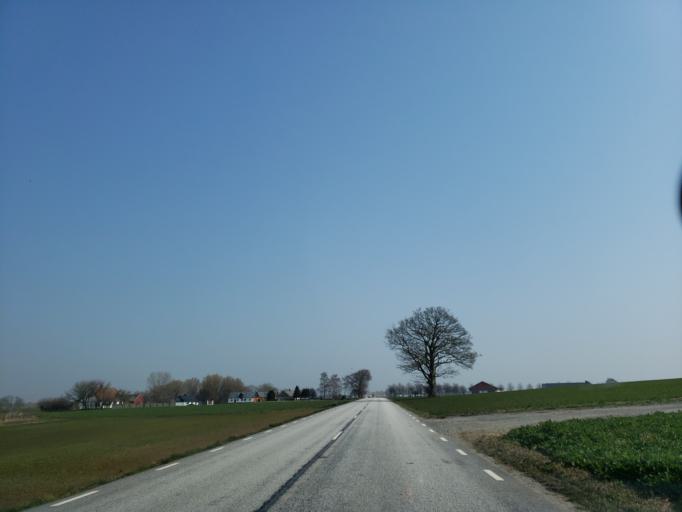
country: SE
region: Skane
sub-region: Simrishamns Kommun
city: Simrishamn
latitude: 55.4675
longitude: 14.2131
